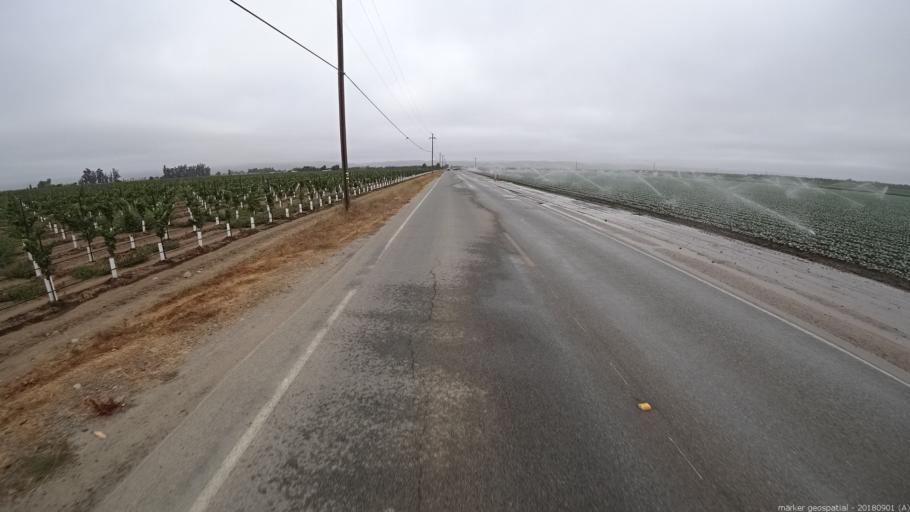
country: US
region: California
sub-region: Monterey County
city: Greenfield
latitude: 36.3009
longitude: -121.2713
